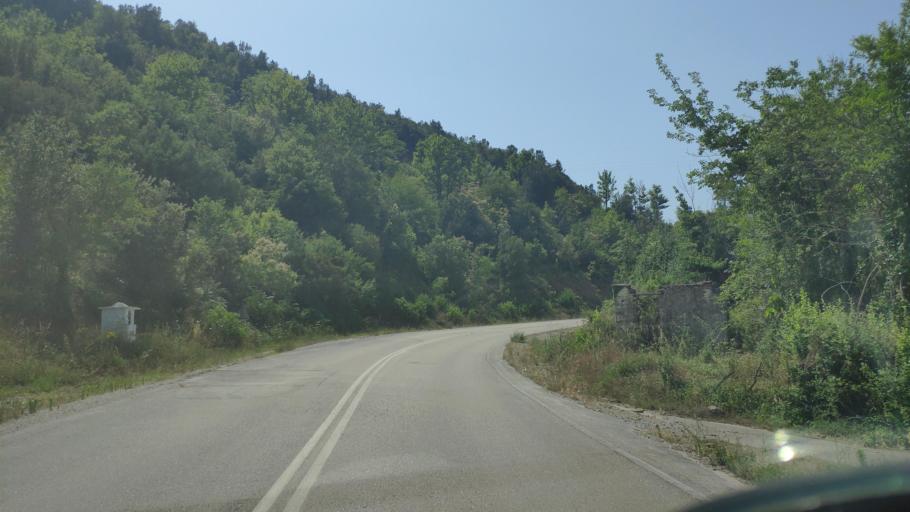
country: GR
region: Epirus
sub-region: Nomos Artas
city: Ano Kalentini
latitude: 39.2255
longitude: 21.1518
